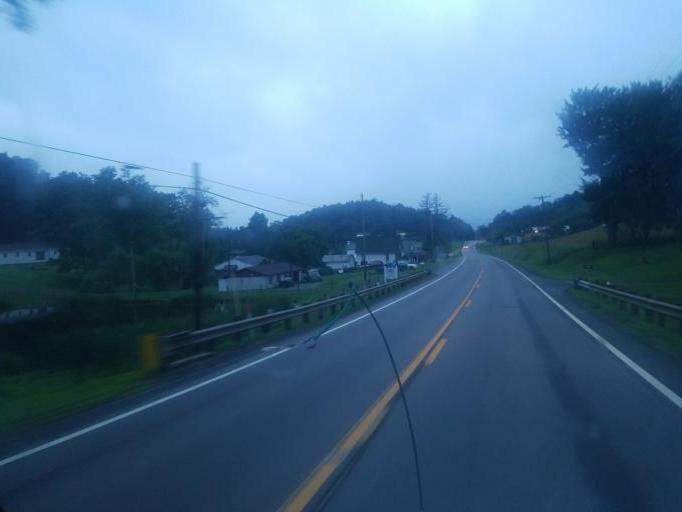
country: US
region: Ohio
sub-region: Carroll County
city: Carrollton
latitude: 40.5531
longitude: -81.0503
